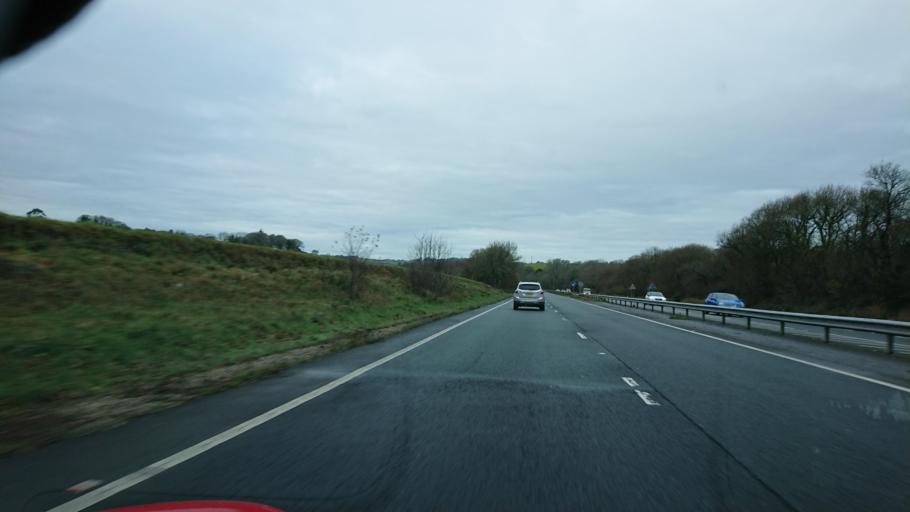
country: GB
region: England
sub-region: Cornwall
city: Pillaton
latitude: 50.4126
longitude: -4.3722
